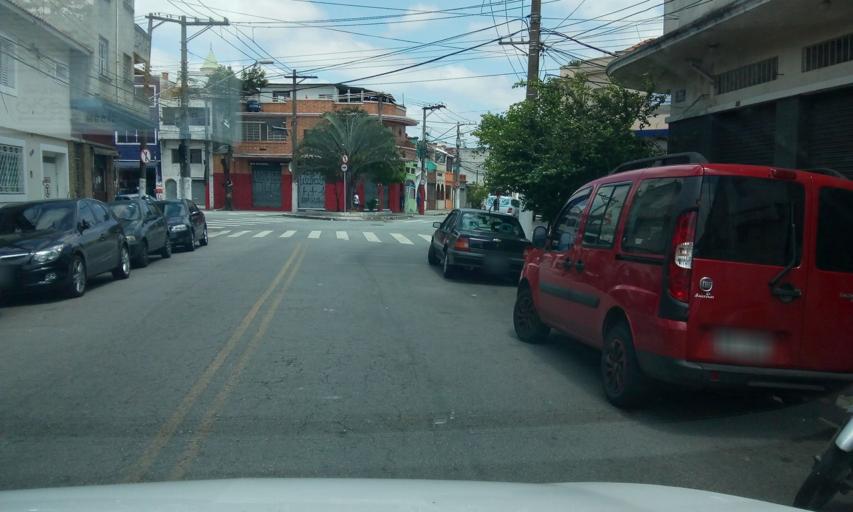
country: BR
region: Sao Paulo
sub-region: Sao Paulo
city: Sao Paulo
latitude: -23.5259
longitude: -46.6061
